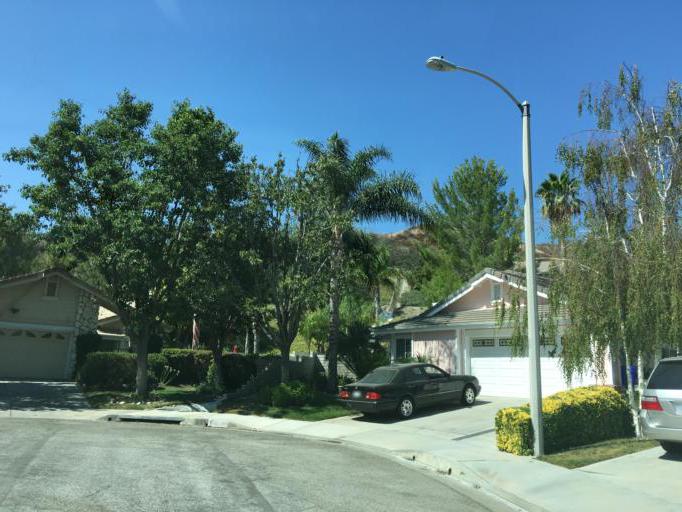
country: US
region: California
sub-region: Los Angeles County
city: Santa Clarita
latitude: 34.3891
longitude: -118.5843
